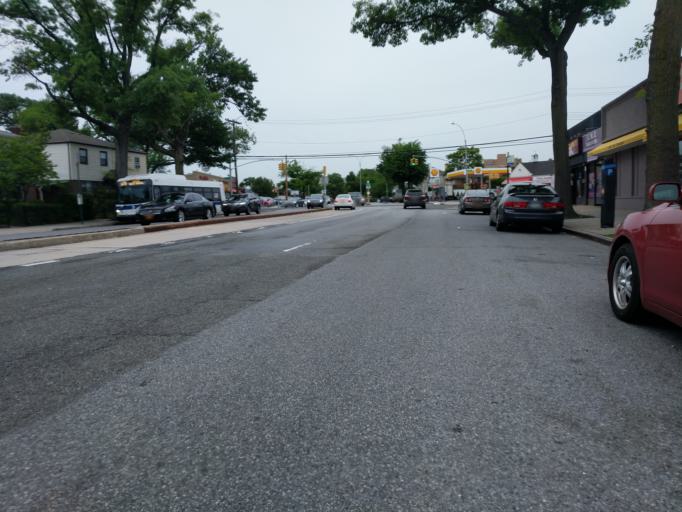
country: US
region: New York
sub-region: Nassau County
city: East Atlantic Beach
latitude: 40.7528
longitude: -73.7802
